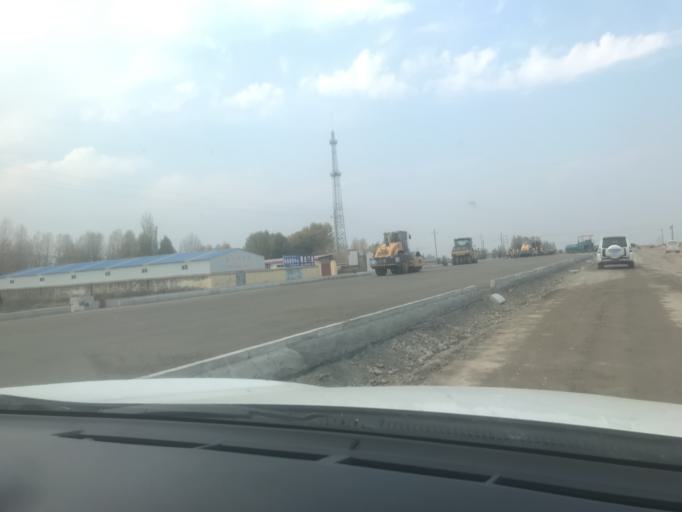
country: CN
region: Gansu Sheng
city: Gulang
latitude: 37.5154
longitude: 102.9008
